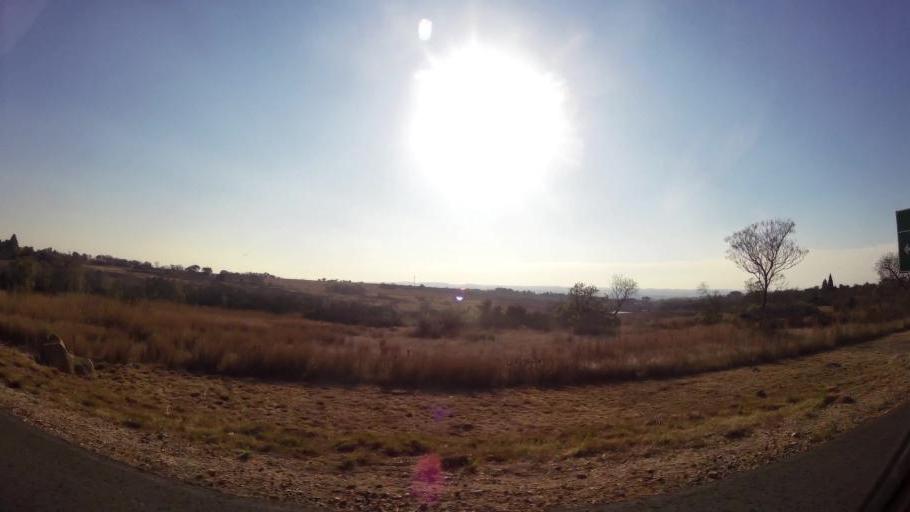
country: ZA
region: Gauteng
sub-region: West Rand District Municipality
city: Muldersdriseloop
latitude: -25.9837
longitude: 27.9238
